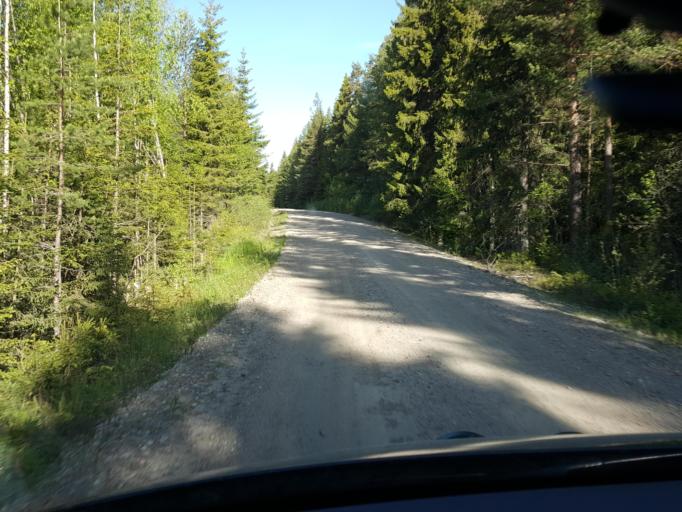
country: SE
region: Vaesternorrland
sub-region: Ange Kommun
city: Ange
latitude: 62.1842
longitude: 15.6135
